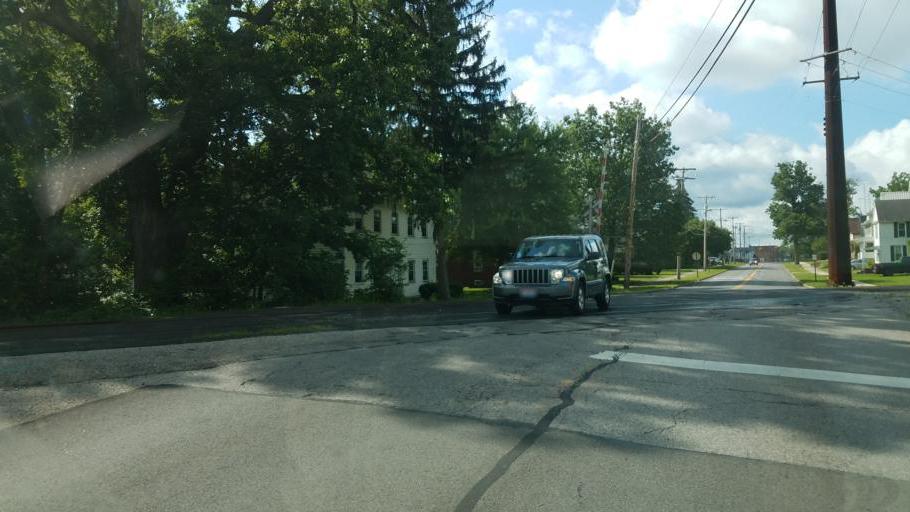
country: US
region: Ohio
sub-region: Richland County
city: Shelby
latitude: 40.8853
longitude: -82.6620
